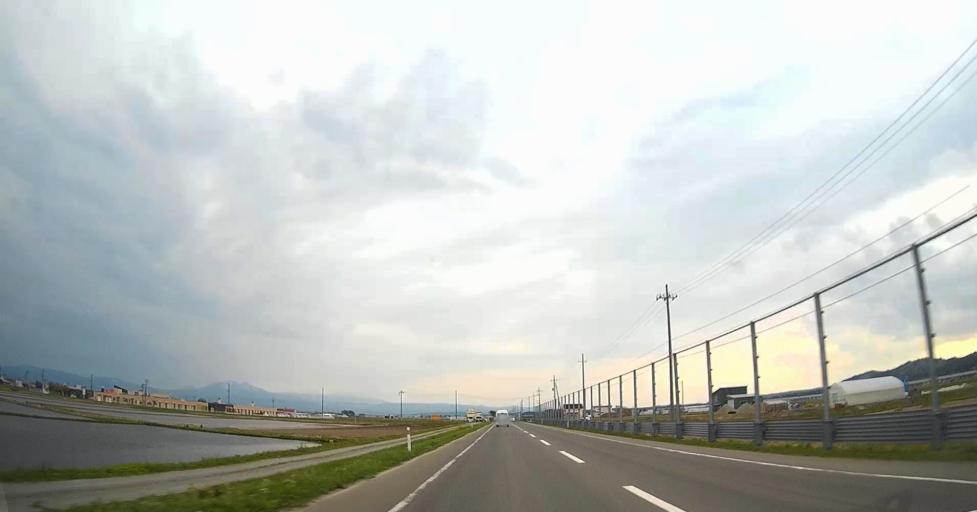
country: JP
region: Aomori
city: Aomori Shi
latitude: 40.8901
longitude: 140.6690
